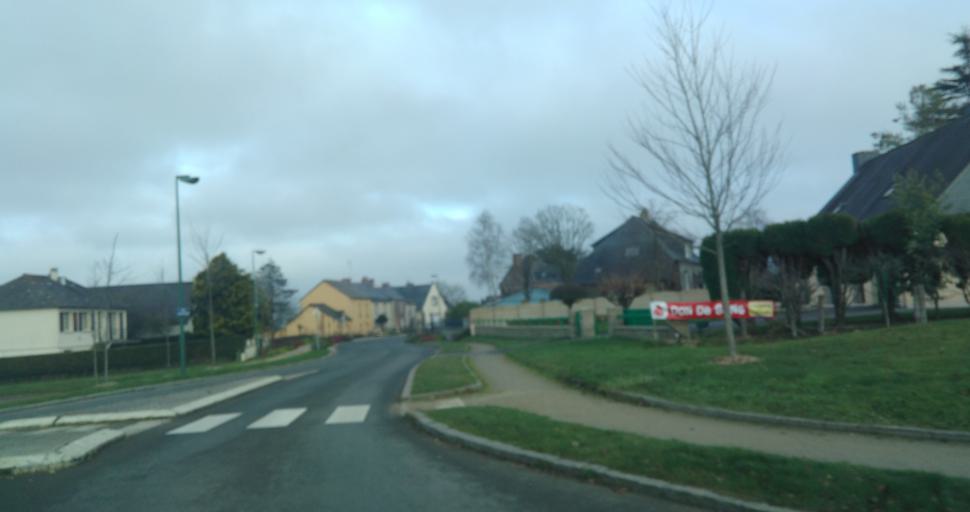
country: FR
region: Brittany
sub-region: Departement d'Ille-et-Vilaine
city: Boisgervilly
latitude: 48.1660
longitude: -2.0695
